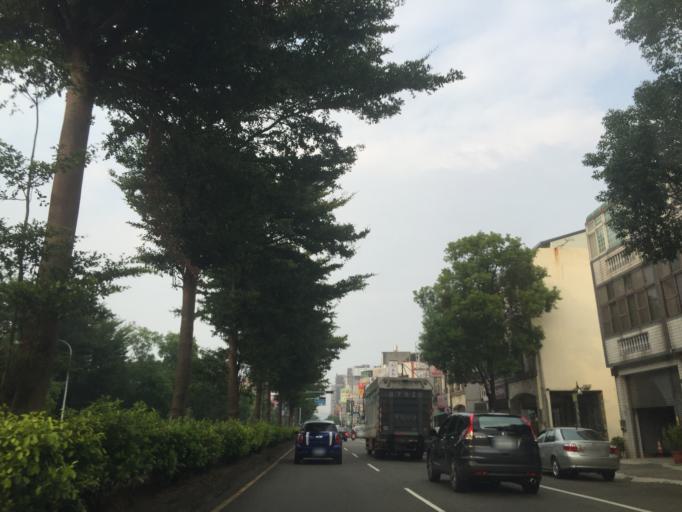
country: TW
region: Taiwan
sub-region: Hsinchu
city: Zhubei
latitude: 24.8271
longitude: 121.0161
